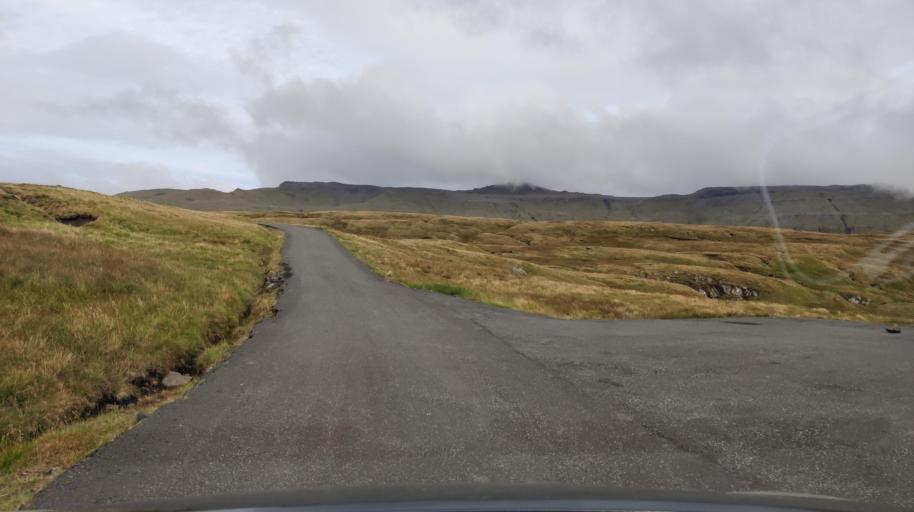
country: FO
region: Streymoy
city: Vestmanna
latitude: 62.1580
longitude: -7.1027
